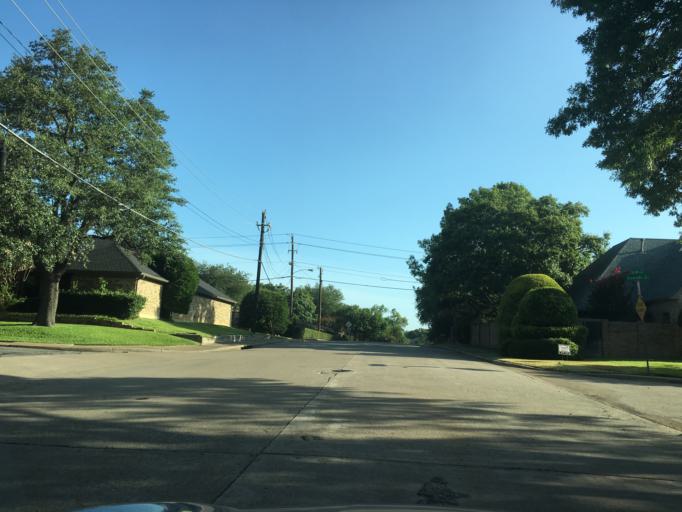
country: US
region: Texas
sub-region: Dallas County
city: Richardson
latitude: 32.8912
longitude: -96.7369
